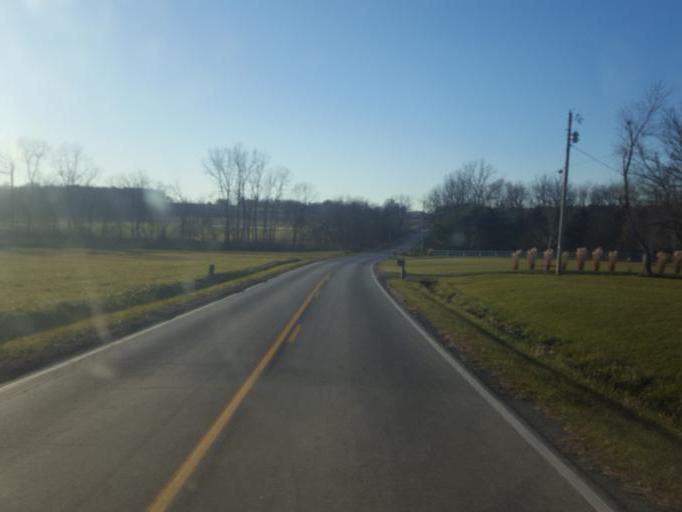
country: US
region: Ohio
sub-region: Ashland County
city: Ashland
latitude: 40.8082
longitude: -82.1614
